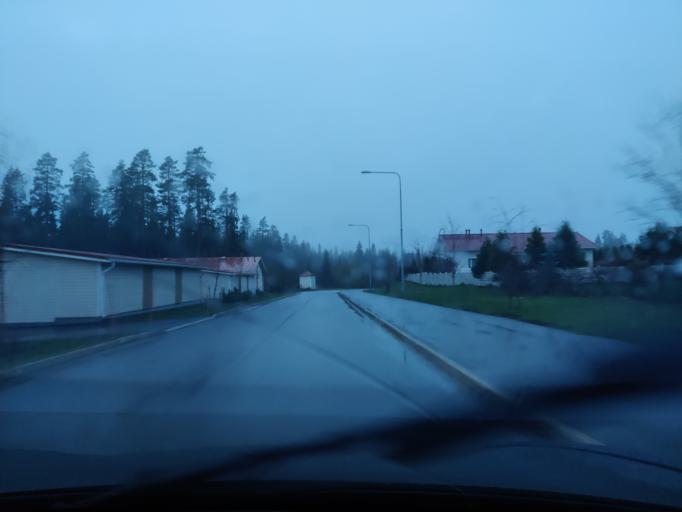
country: FI
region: Northern Savo
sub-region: Kuopio
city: Kuopio
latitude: 62.8283
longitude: 27.7189
